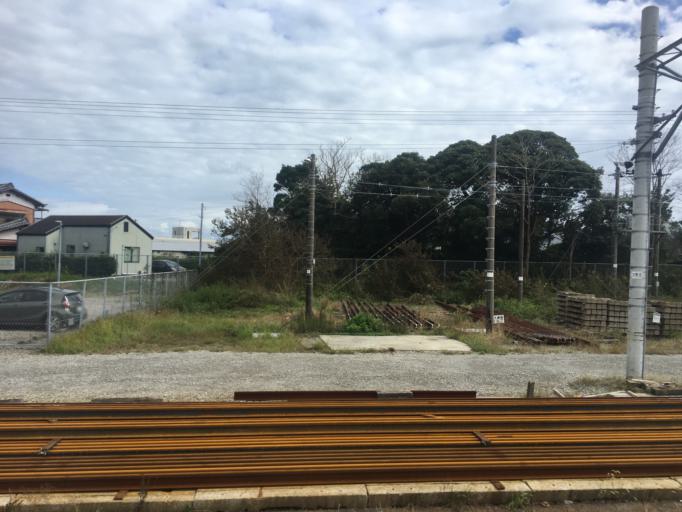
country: JP
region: Chiba
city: Ohara
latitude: 35.2528
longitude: 140.3910
